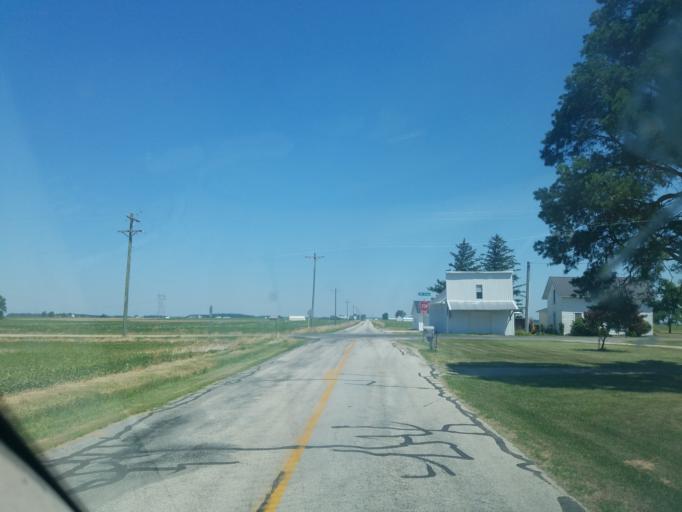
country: US
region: Ohio
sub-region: Mercer County
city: Rockford
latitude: 40.6108
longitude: -84.7085
